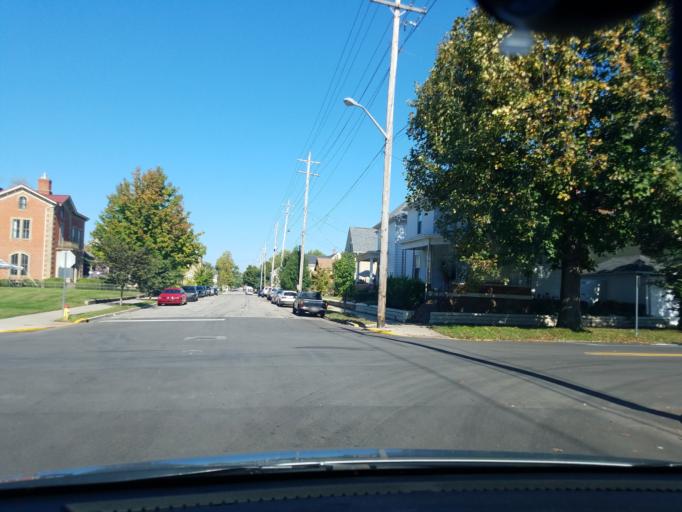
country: US
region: Indiana
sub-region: Floyd County
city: New Albany
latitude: 38.2874
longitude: -85.8142
